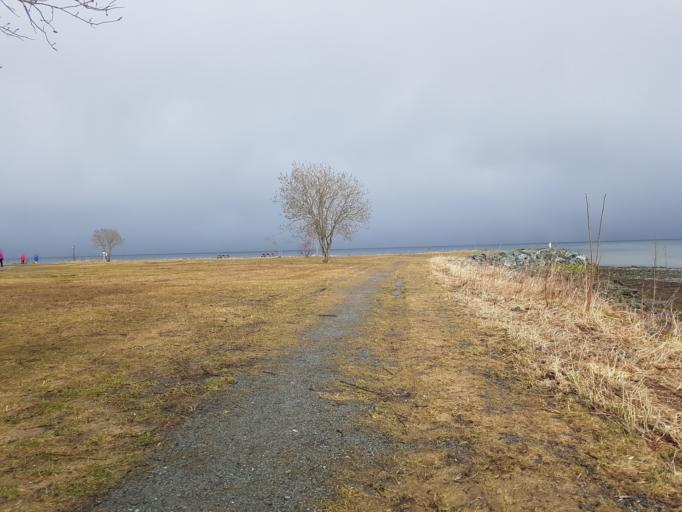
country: NO
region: Sor-Trondelag
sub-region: Trondheim
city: Trondheim
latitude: 63.4311
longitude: 10.5207
